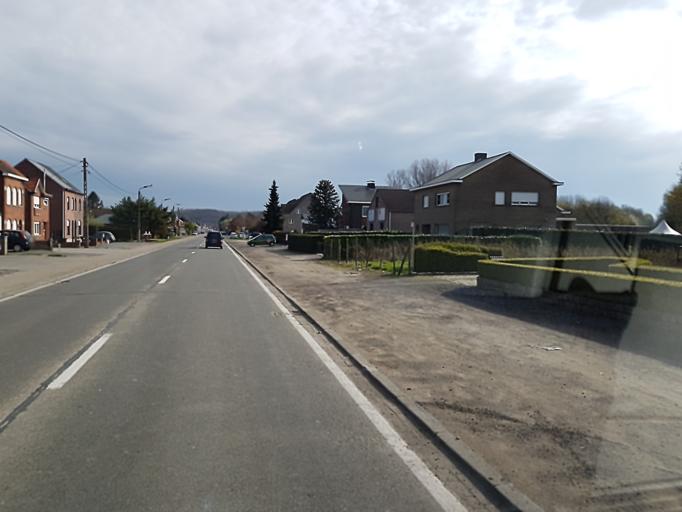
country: BE
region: Flanders
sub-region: Provincie Vlaams-Brabant
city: Holsbeek
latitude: 50.9427
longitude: 4.7426
